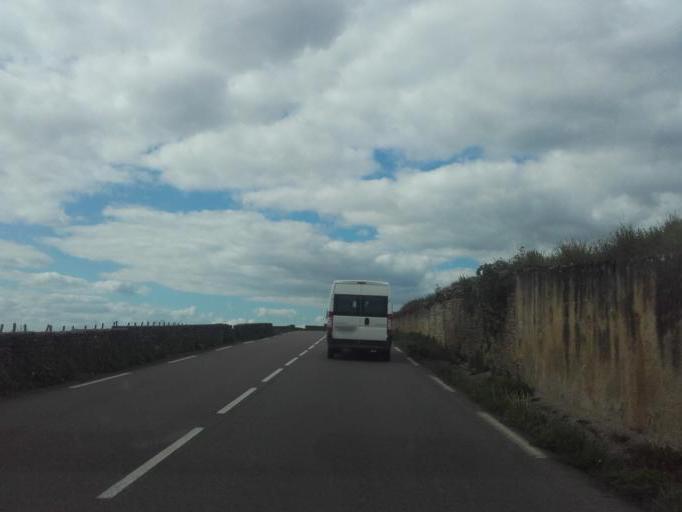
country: FR
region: Bourgogne
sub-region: Departement de la Cote-d'Or
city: Meursault
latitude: 46.9968
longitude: 4.7817
